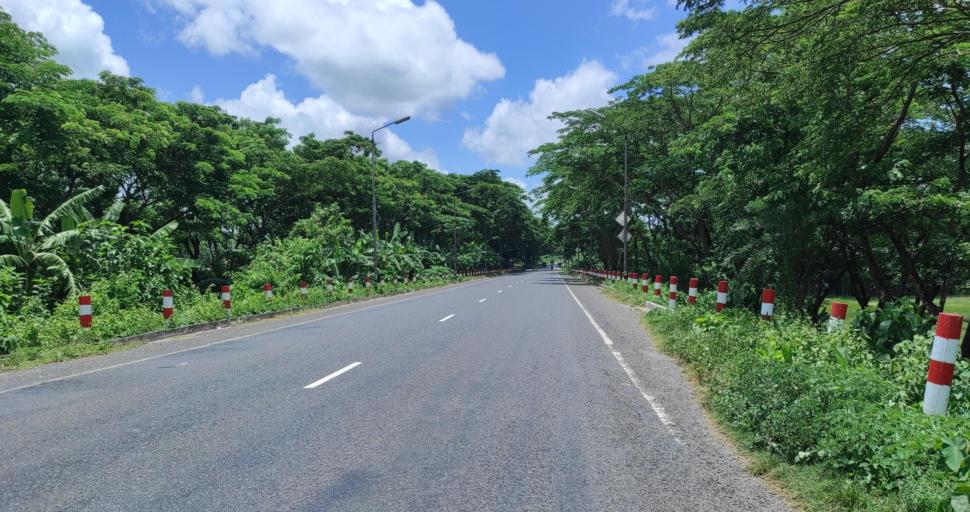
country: BD
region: Barisal
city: Gaurnadi
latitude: 22.8230
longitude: 90.2657
